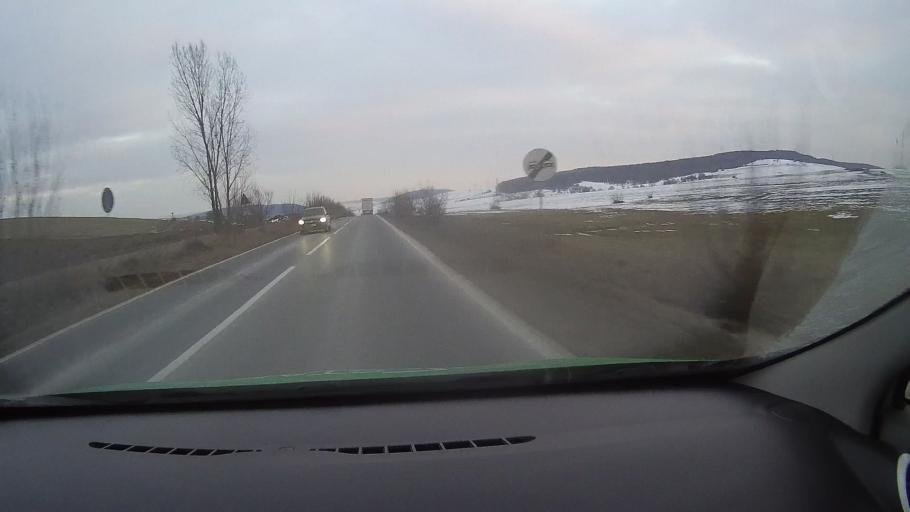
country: RO
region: Harghita
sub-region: Comuna Lupeni
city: Lupeni
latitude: 46.3584
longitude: 25.2503
